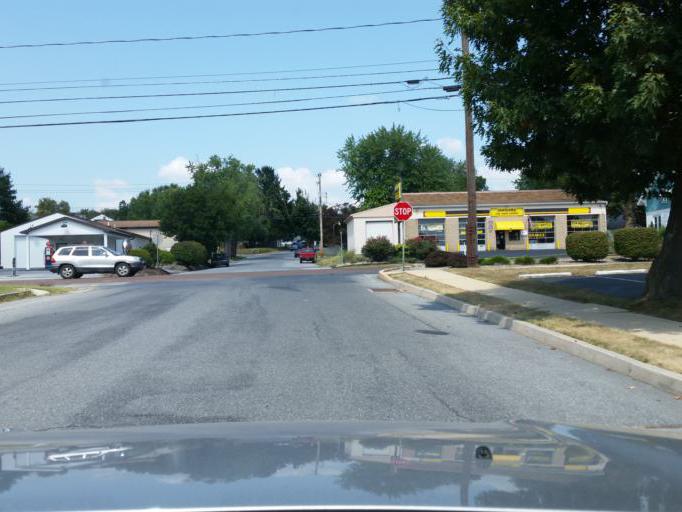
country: US
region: Pennsylvania
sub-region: Dauphin County
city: Palmdale
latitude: 40.2973
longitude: -76.6184
